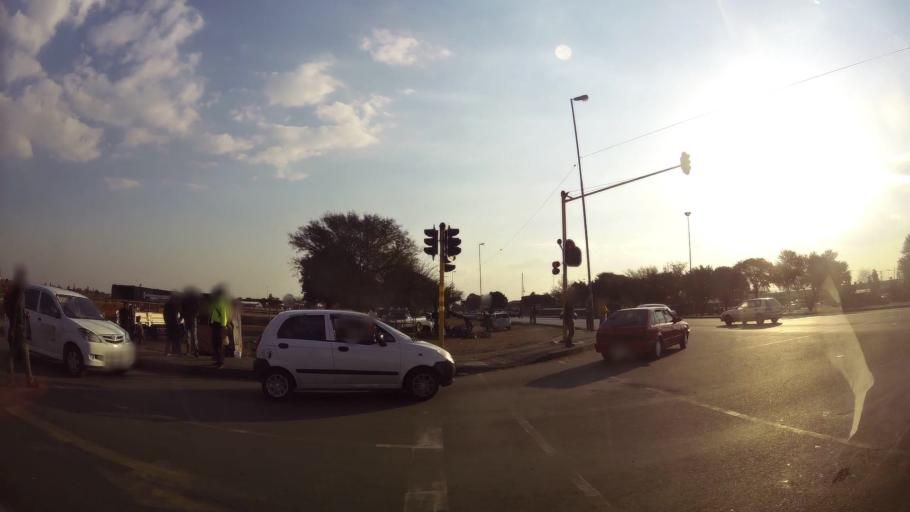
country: ZA
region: Gauteng
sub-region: Ekurhuleni Metropolitan Municipality
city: Germiston
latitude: -26.3426
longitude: 28.2163
